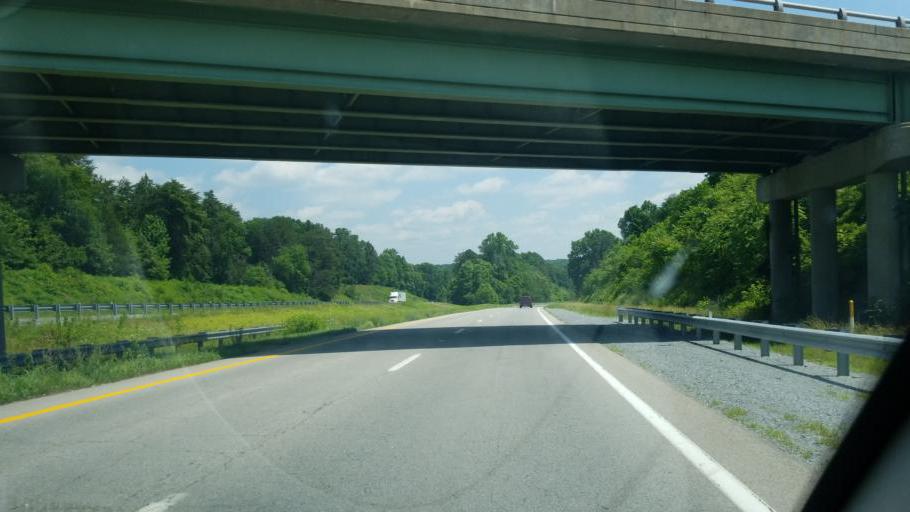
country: US
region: Virginia
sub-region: Pittsylvania County
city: Hurt
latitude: 37.1145
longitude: -79.3267
